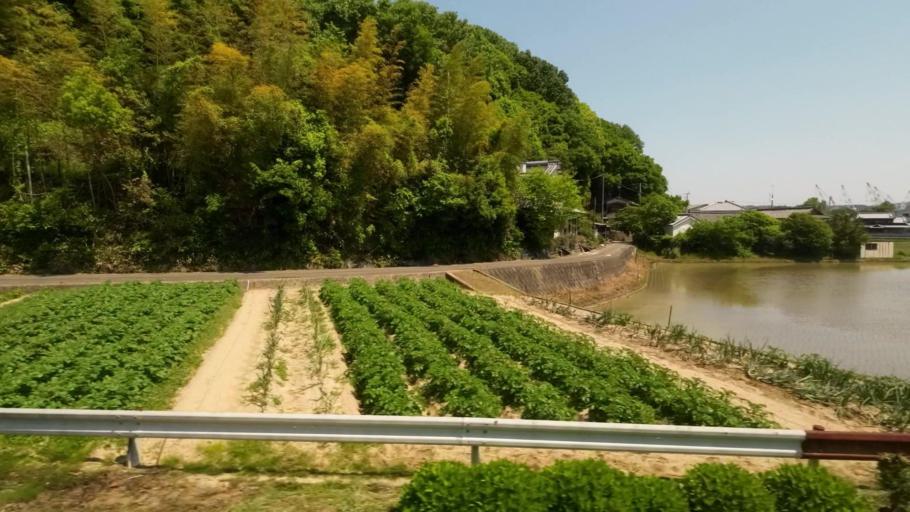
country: JP
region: Ehime
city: Hojo
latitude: 34.0614
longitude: 132.9060
